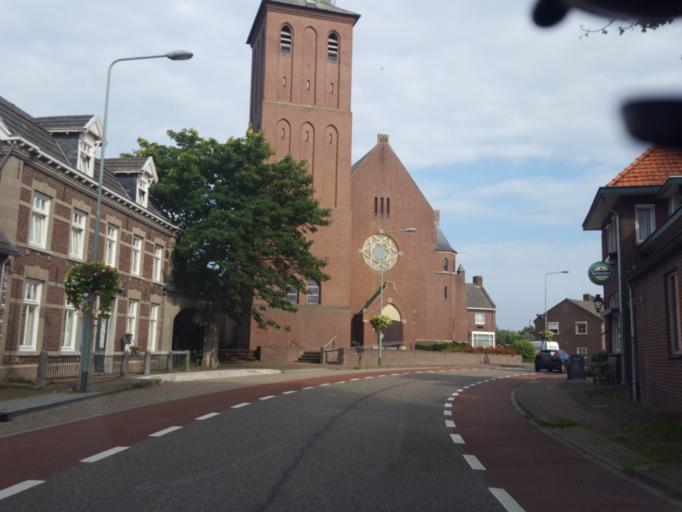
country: NL
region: Limburg
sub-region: Gemeente Bergen
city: Wellerlooi
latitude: 51.5151
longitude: 6.0860
